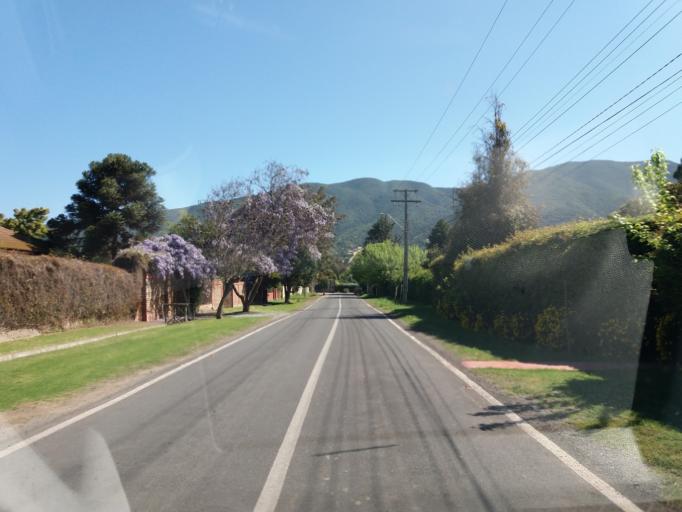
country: CL
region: Valparaiso
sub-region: Provincia de Marga Marga
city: Limache
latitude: -33.0008
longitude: -71.1925
